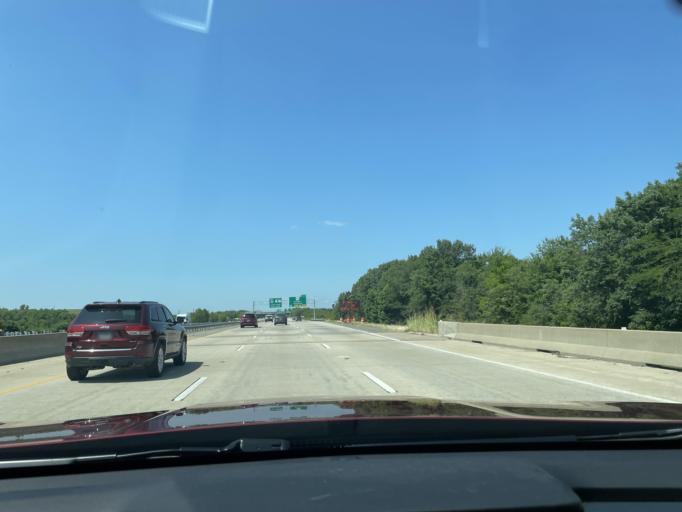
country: US
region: Arkansas
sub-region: Pulaski County
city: Jacksonville
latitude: 34.8503
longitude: -92.1442
